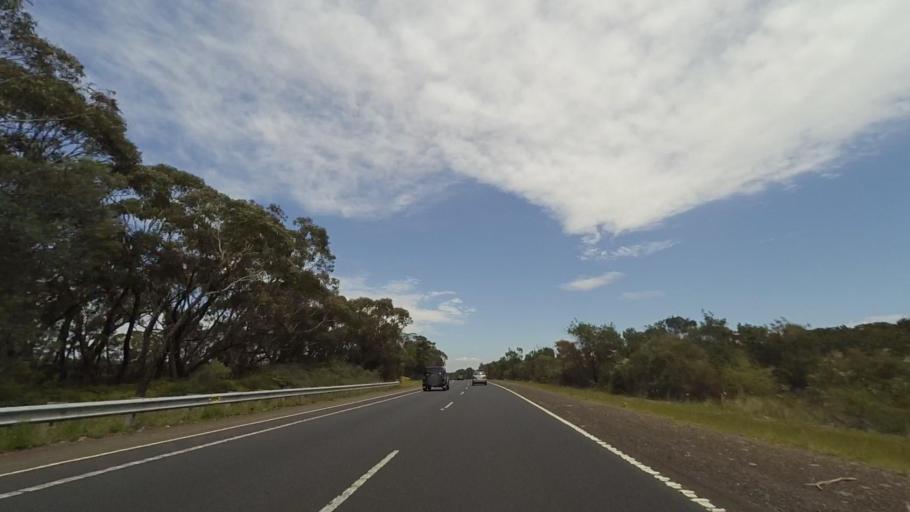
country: AU
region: New South Wales
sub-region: Wollongong
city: Helensburgh
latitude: -34.2460
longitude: 150.9393
